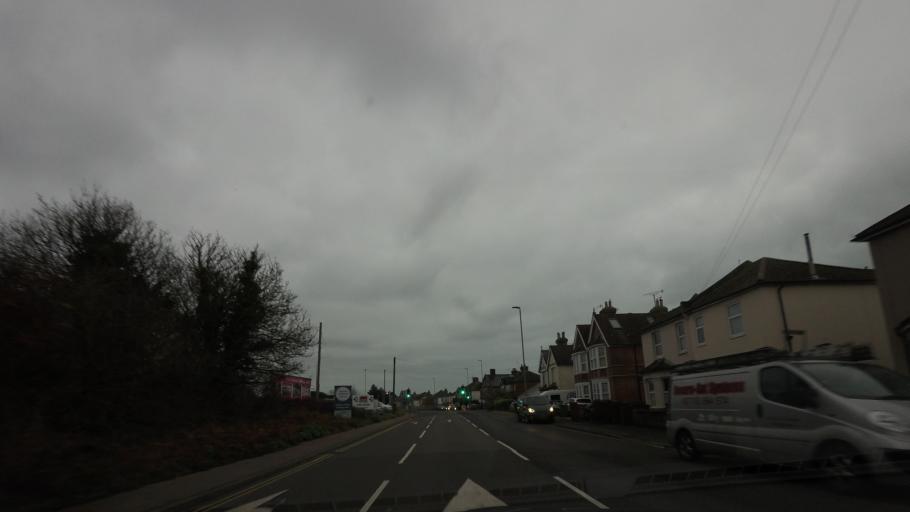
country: GB
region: England
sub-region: East Sussex
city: Saint Leonards-on-Sea
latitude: 50.8511
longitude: 0.5253
